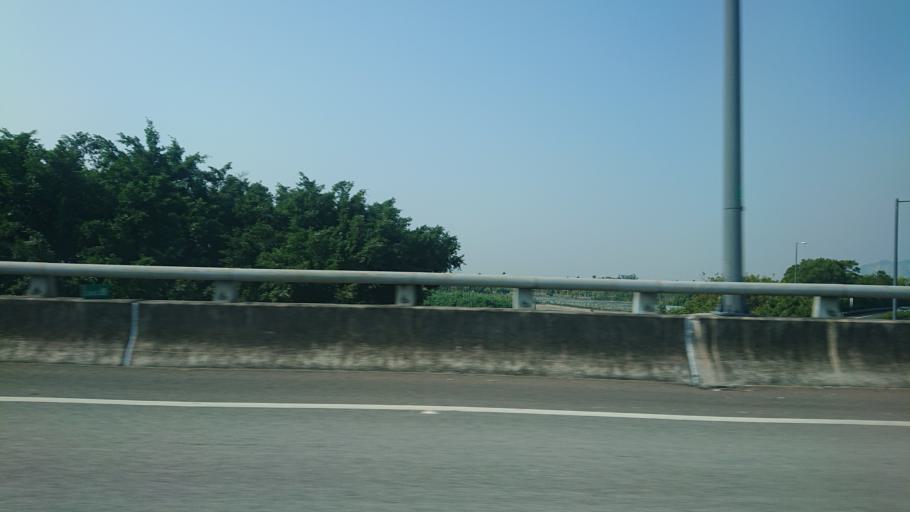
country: TW
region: Taiwan
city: Lugu
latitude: 23.7957
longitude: 120.7019
